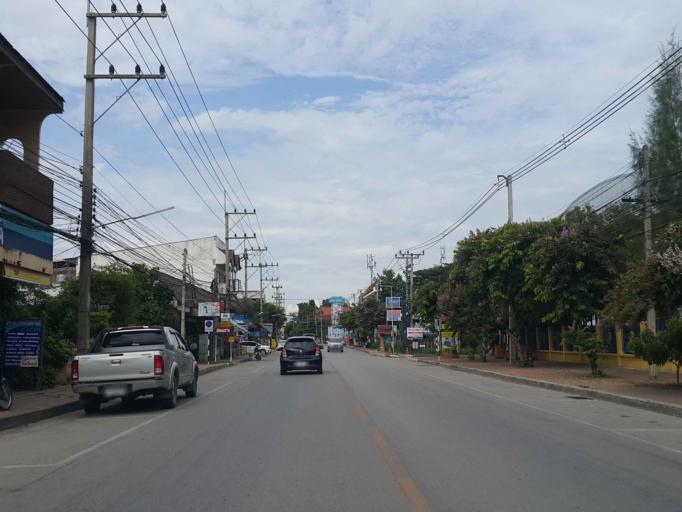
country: TH
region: Lamphun
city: Lamphun
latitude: 18.5922
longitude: 99.0136
